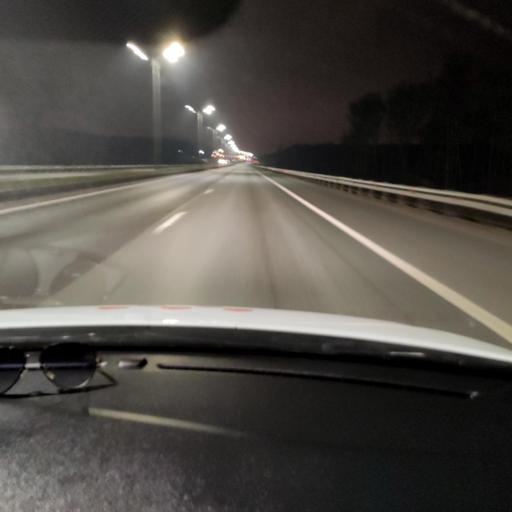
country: RU
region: Tatarstan
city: Stolbishchi
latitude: 55.7154
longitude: 49.2085
